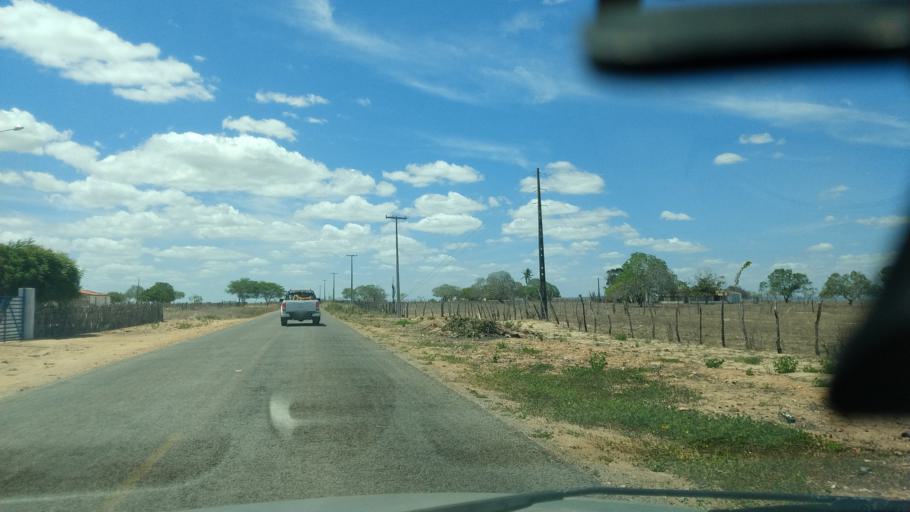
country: BR
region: Rio Grande do Norte
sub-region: Sao Paulo Do Potengi
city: Sao Paulo do Potengi
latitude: -5.9148
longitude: -35.7391
